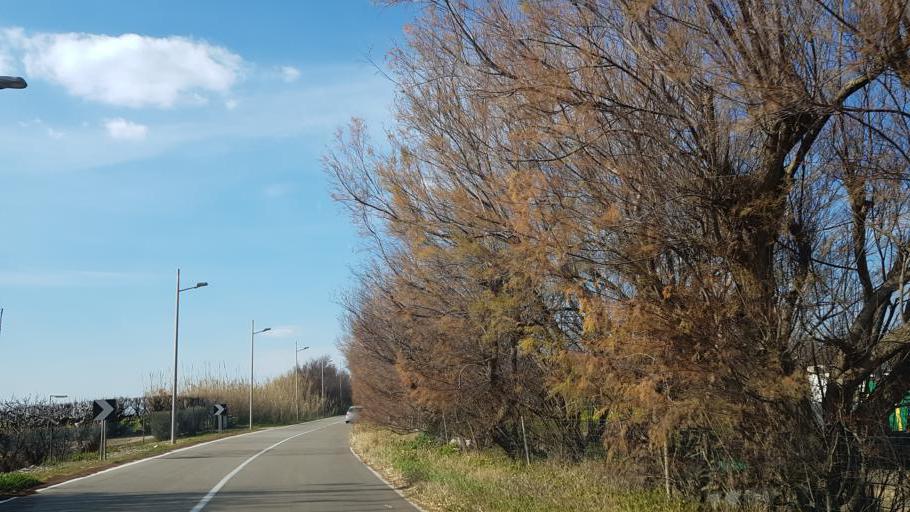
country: IT
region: Apulia
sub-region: Provincia di Brindisi
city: Brindisi
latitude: 40.6809
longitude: 17.8928
